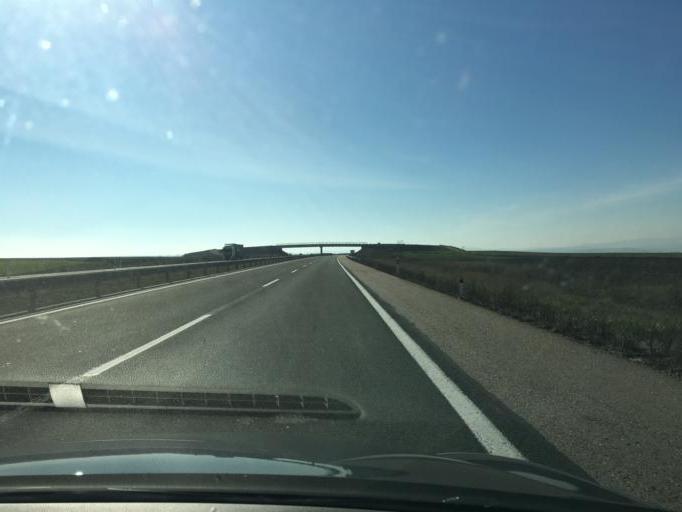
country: ES
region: Castille and Leon
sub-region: Provincia de Burgos
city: Grisalena
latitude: 42.5679
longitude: -3.2636
